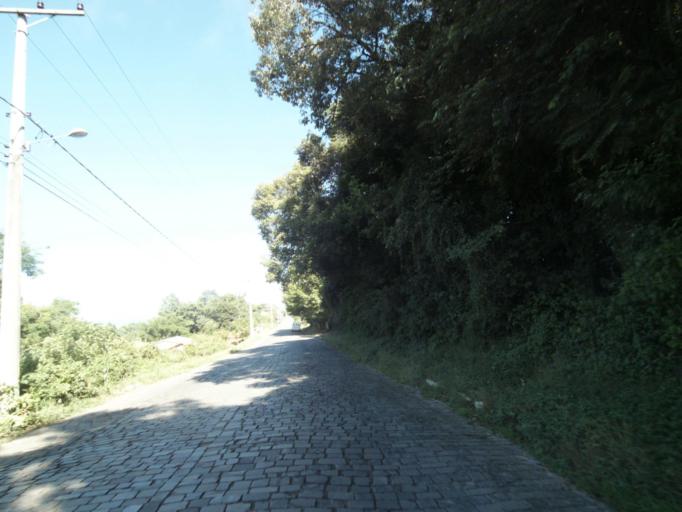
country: BR
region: Rio Grande do Sul
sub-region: Bento Goncalves
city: Bento Goncalves
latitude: -29.1186
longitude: -51.5659
